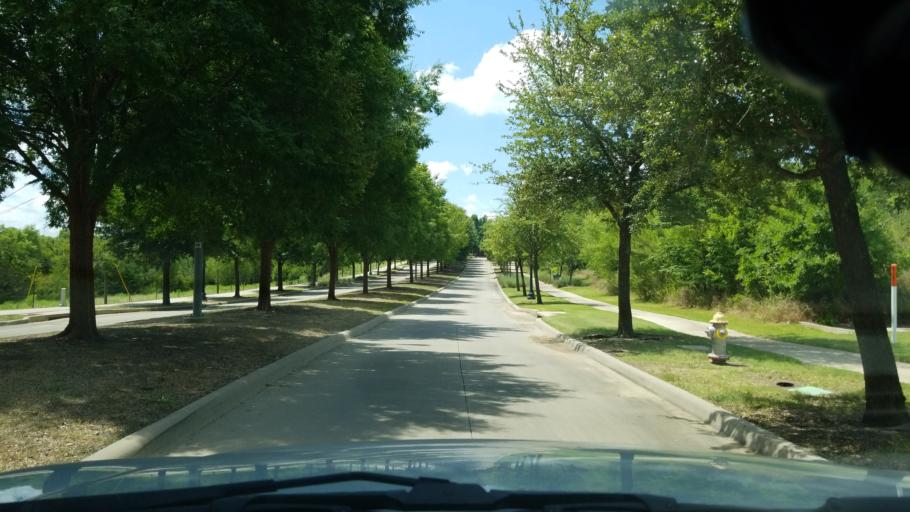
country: US
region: Texas
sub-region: Dallas County
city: Duncanville
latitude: 32.6980
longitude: -96.9428
